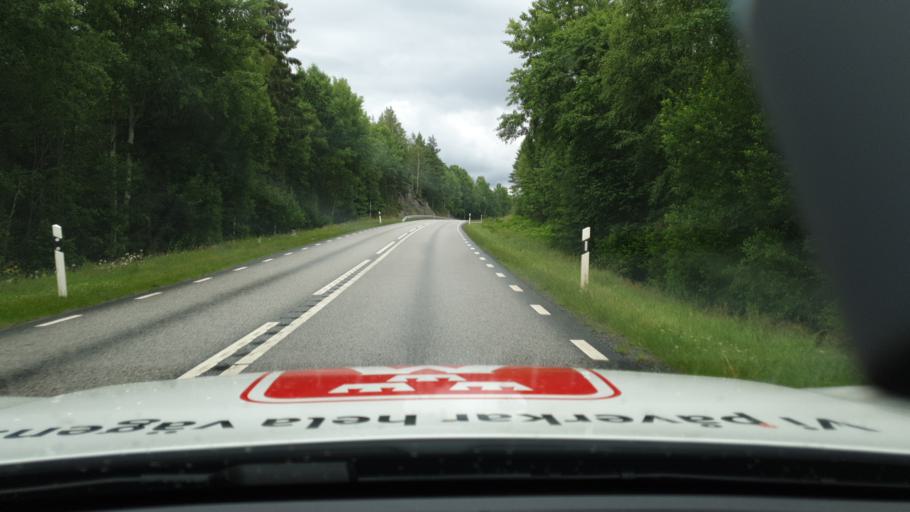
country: SE
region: Joenkoeping
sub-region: Jonkopings Kommun
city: Tenhult
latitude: 57.7105
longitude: 14.3443
